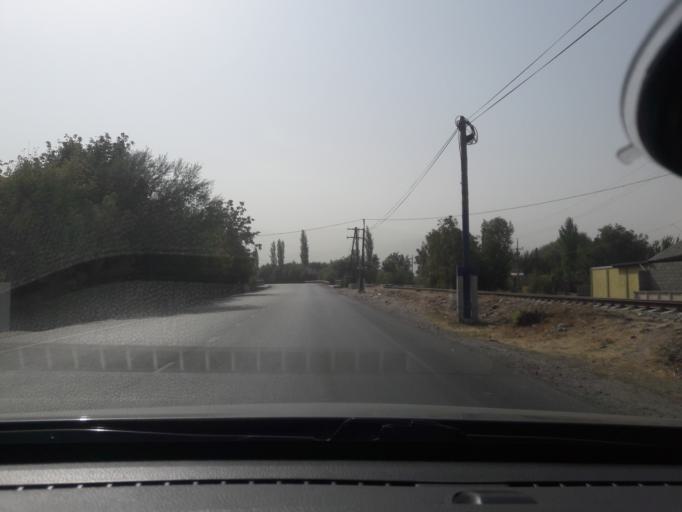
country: TJ
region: Republican Subordination
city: Vahdat
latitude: 38.5216
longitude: 69.0285
